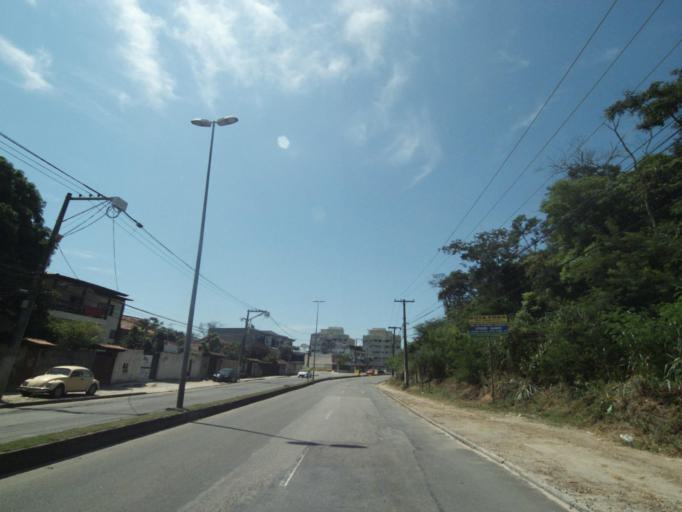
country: BR
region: Rio de Janeiro
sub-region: Sao Goncalo
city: Sao Goncalo
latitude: -22.8862
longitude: -43.0327
